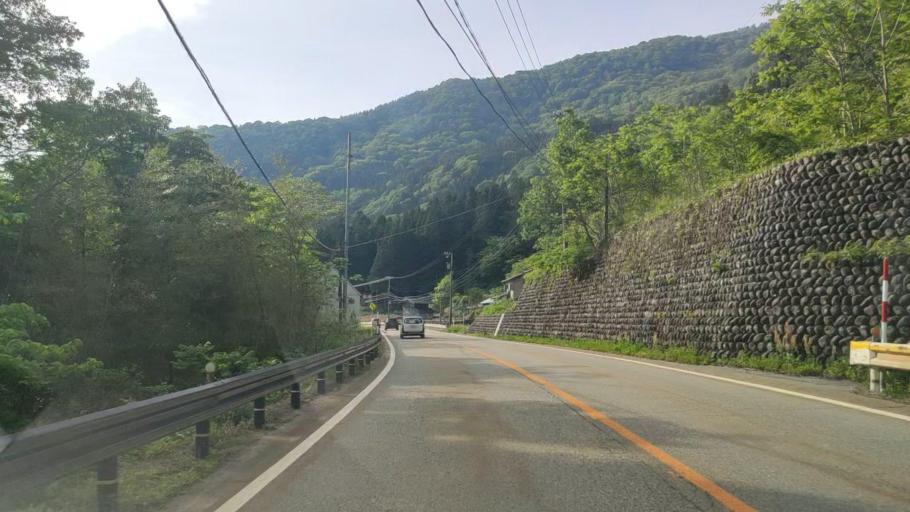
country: JP
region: Toyama
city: Yatsuomachi-higashikumisaka
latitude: 36.4483
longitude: 137.2723
